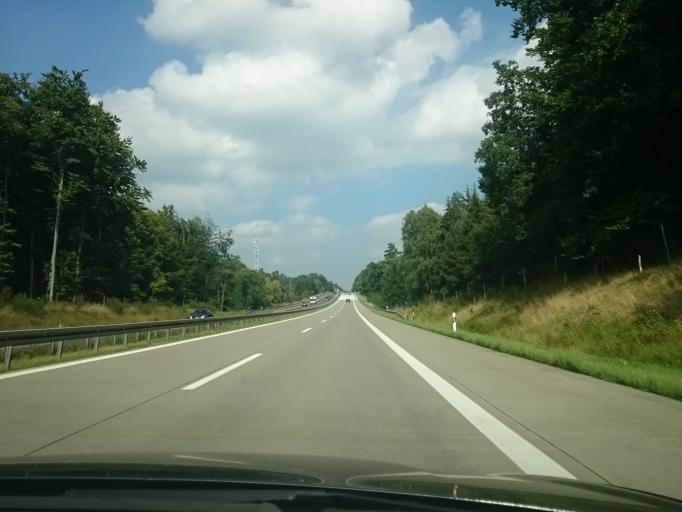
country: DE
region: Brandenburg
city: Althuttendorf
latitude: 53.0187
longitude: 13.8277
